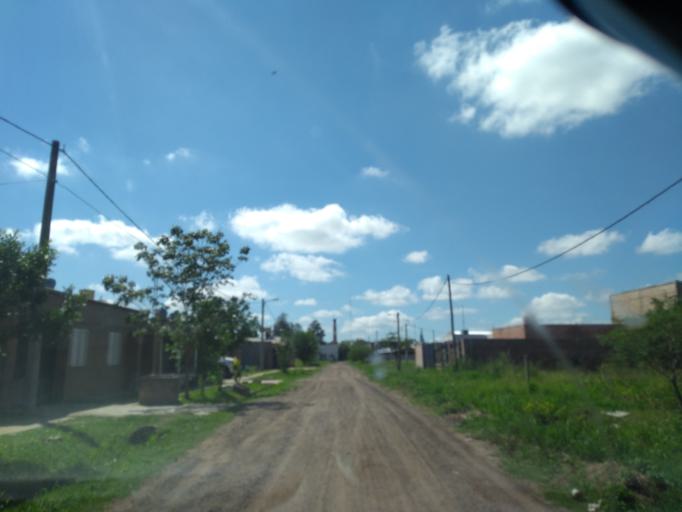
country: AR
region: Chaco
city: Fontana
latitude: -27.4144
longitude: -59.0370
